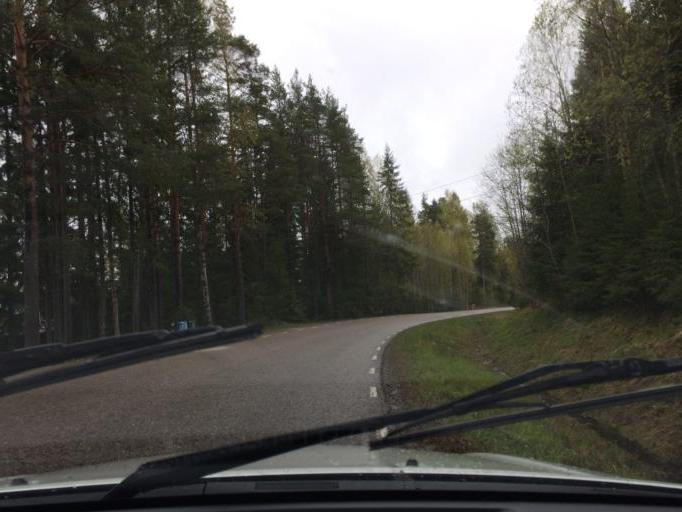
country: SE
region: Dalarna
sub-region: Ludvika Kommun
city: Abborrberget
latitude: 60.0663
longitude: 14.8700
